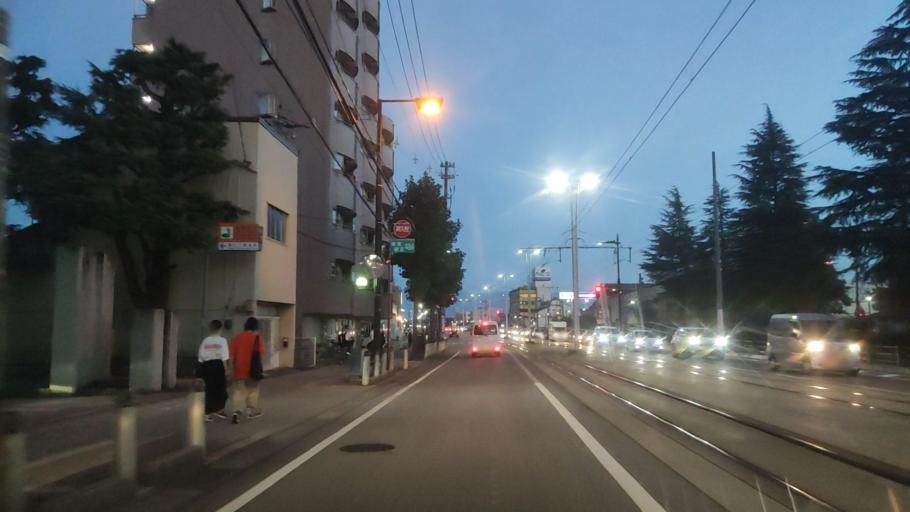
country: JP
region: Toyama
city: Toyama-shi
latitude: 36.6976
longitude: 137.1922
